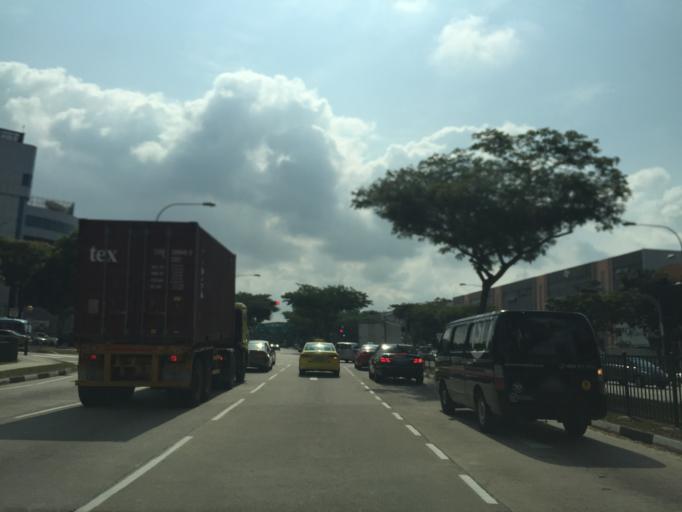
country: SG
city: Singapore
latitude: 1.3355
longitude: 103.8935
